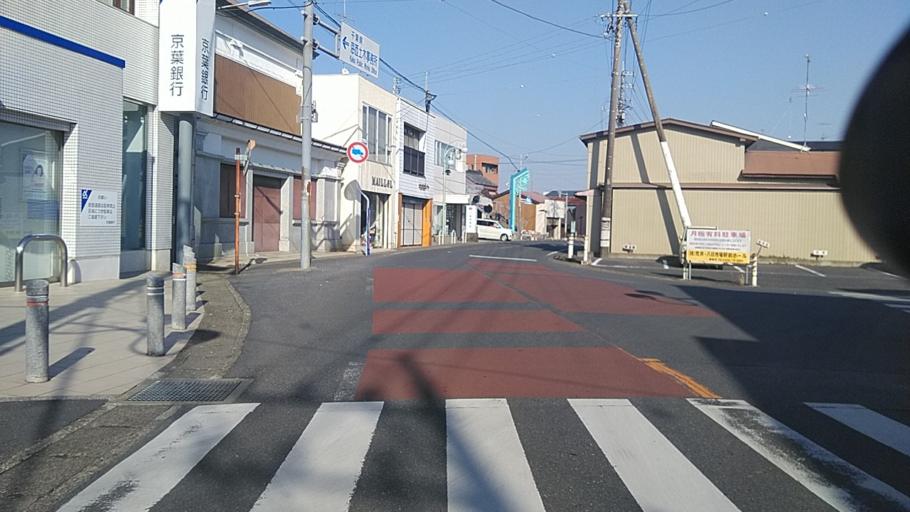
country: JP
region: Chiba
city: Yokaichiba
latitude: 35.7008
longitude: 140.5468
